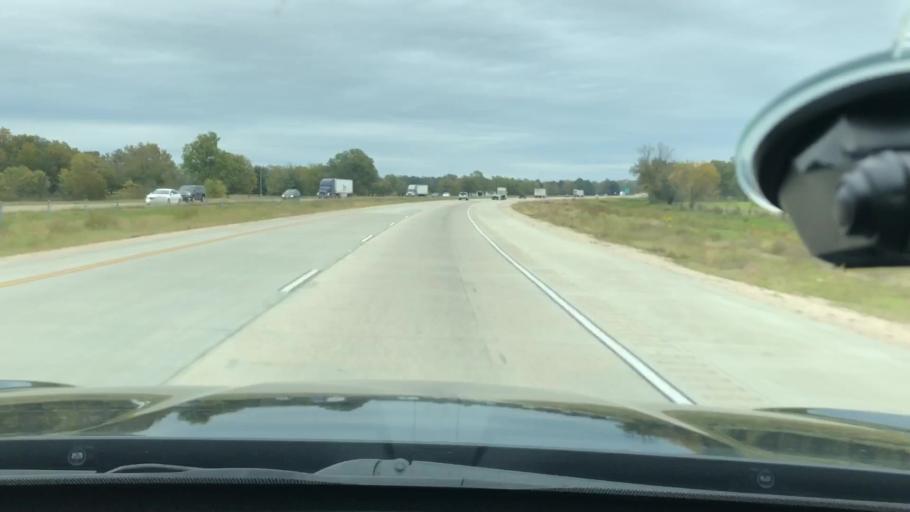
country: US
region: Arkansas
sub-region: Miller County
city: Texarkana
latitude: 33.5472
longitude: -93.8874
